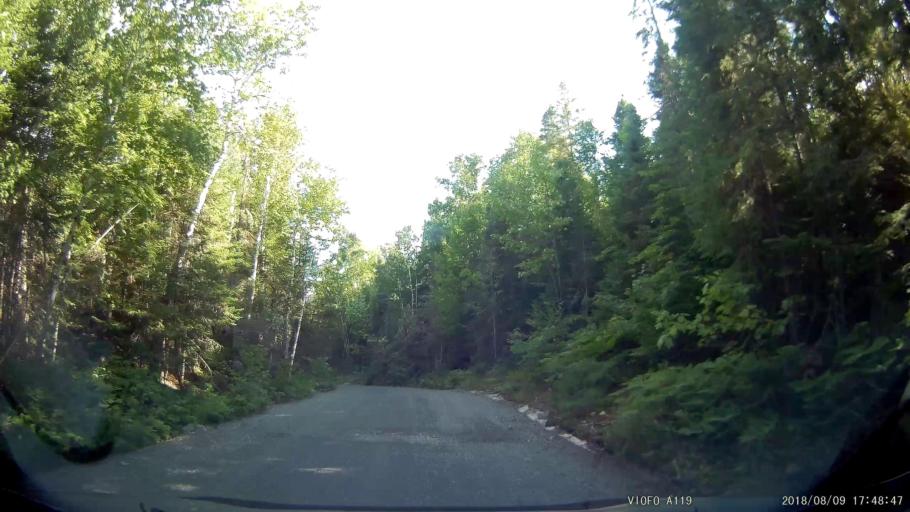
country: CA
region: Ontario
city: Rayside-Balfour
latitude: 46.5887
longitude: -81.5407
